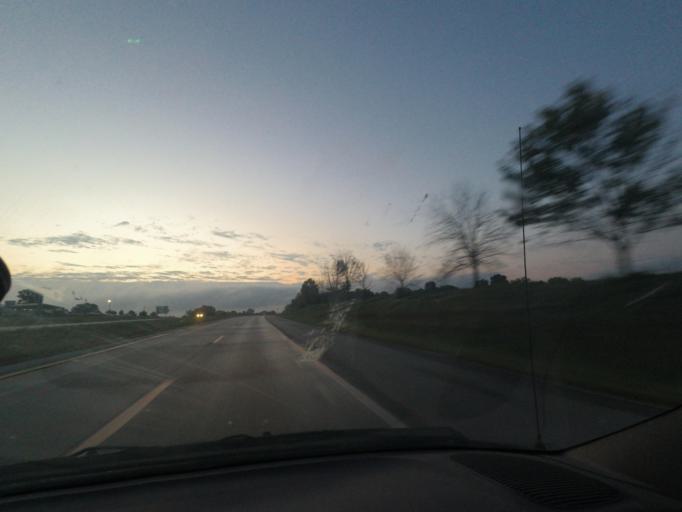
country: US
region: Missouri
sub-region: Linn County
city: Brookfield
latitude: 39.7708
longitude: -93.0626
